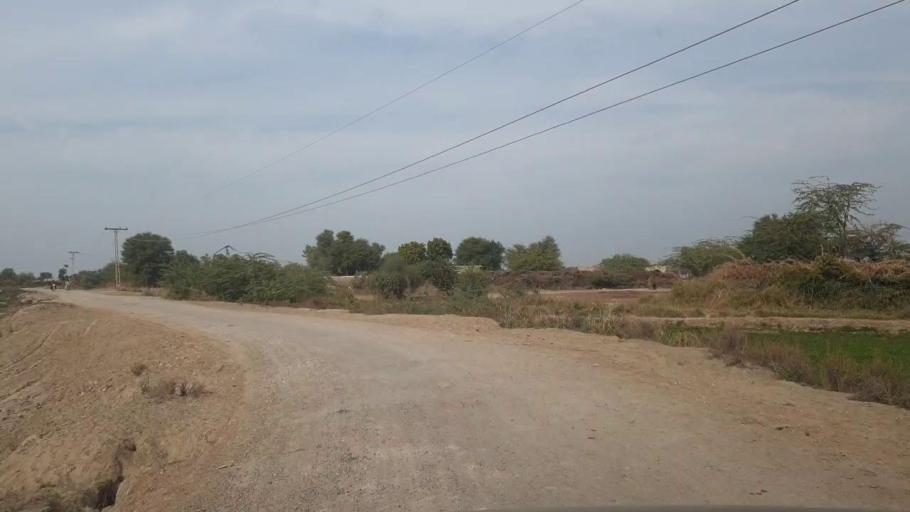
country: PK
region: Sindh
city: Shahpur Chakar
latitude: 26.1063
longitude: 68.5057
